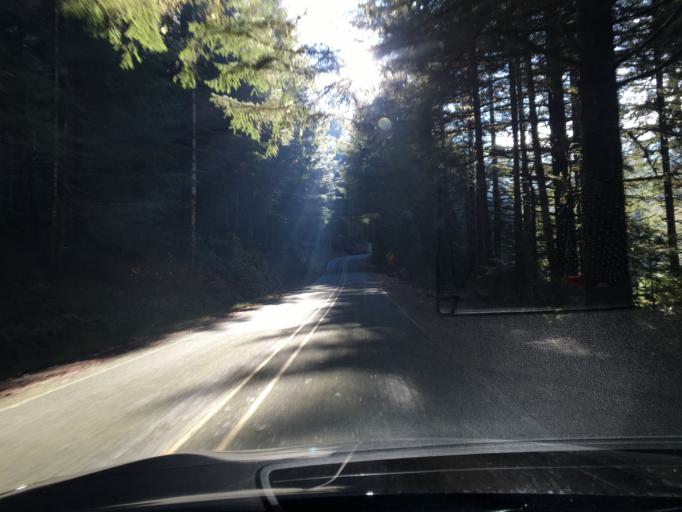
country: US
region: Oregon
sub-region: Douglas County
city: Roseburg
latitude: 43.3343
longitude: -123.5907
